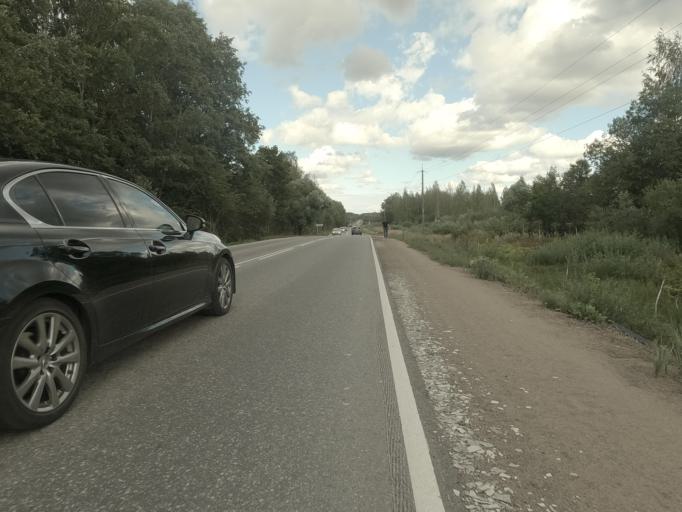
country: RU
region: Leningrad
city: Shcheglovo
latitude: 60.0294
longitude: 30.7677
